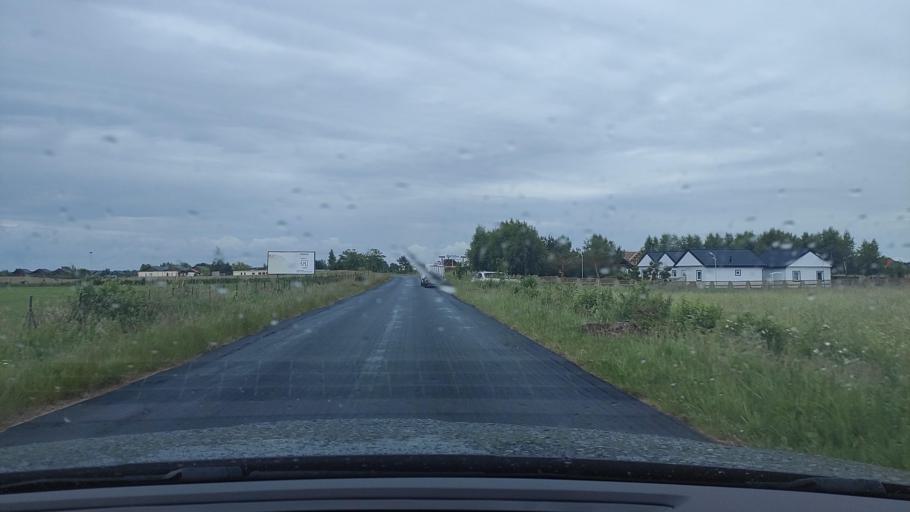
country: PL
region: West Pomeranian Voivodeship
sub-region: Powiat slawienski
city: Slawno
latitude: 54.5297
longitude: 16.5802
